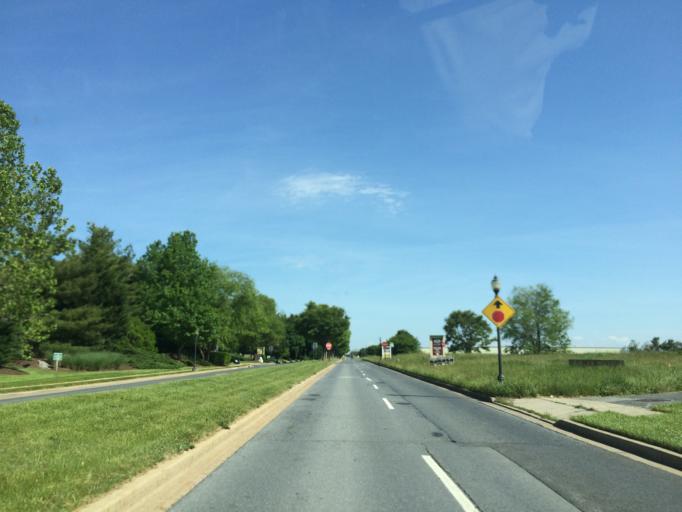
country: US
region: Maryland
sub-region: Frederick County
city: Clover Hill
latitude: 39.4528
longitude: -77.3911
